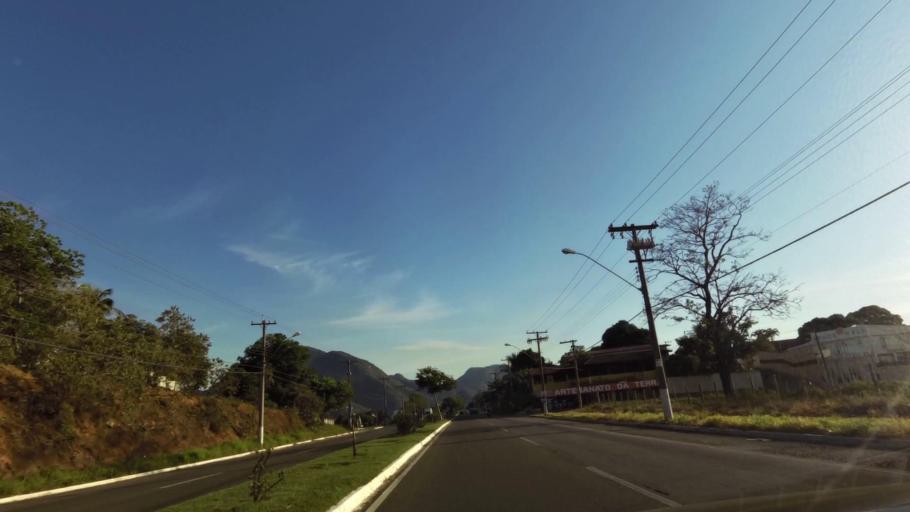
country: BR
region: Espirito Santo
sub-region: Guarapari
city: Guarapari
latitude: -20.6397
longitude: -40.5176
